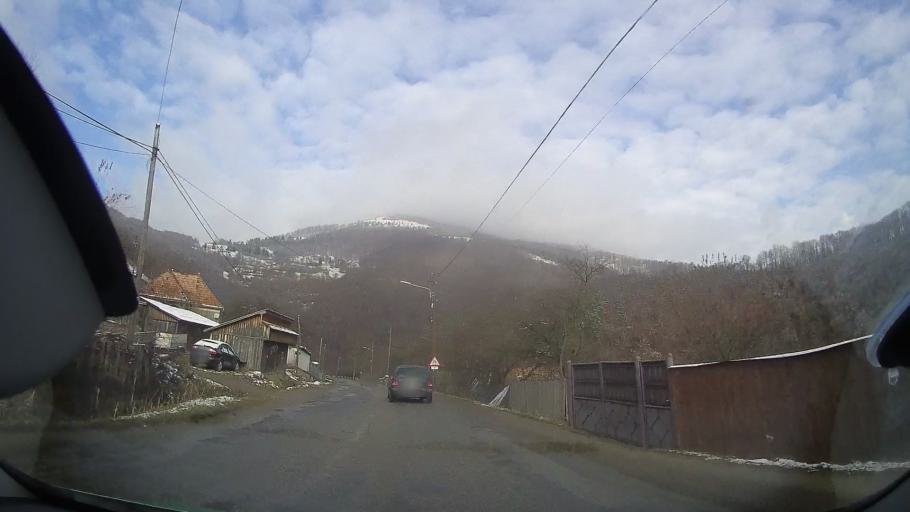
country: RO
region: Alba
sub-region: Oras Baia de Aries
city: Baia de Aries
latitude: 46.3770
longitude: 23.2613
